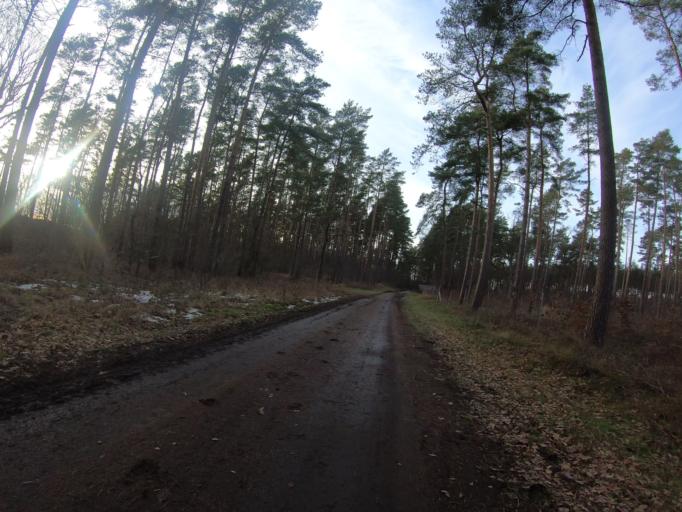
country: DE
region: Lower Saxony
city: Leiferde
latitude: 52.4949
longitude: 10.4598
